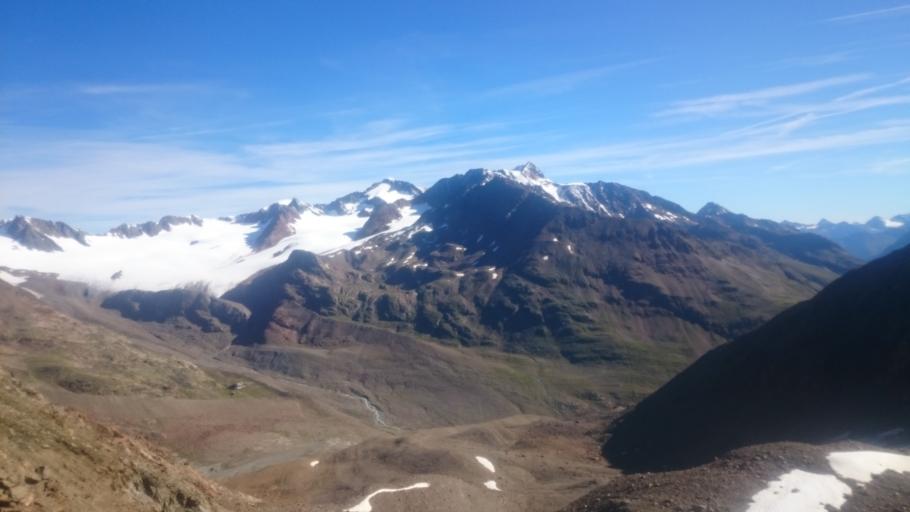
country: IT
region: Trentino-Alto Adige
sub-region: Bolzano
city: Senales
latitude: 46.8376
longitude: 10.8194
